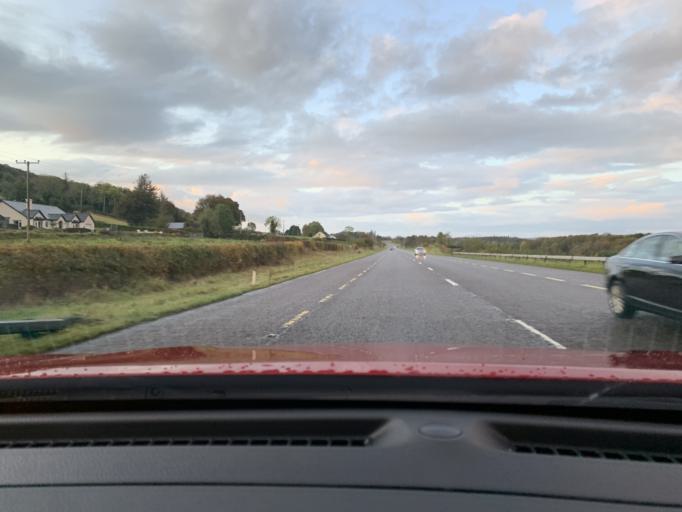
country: IE
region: Connaught
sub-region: Roscommon
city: Boyle
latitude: 54.0424
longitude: -8.3372
